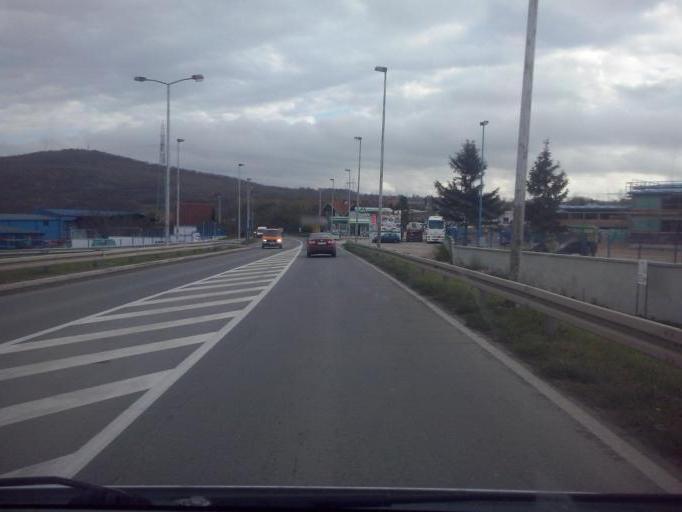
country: RS
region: Central Serbia
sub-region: Pomoravski Okrug
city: Paracin
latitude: 43.8559
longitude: 21.4383
